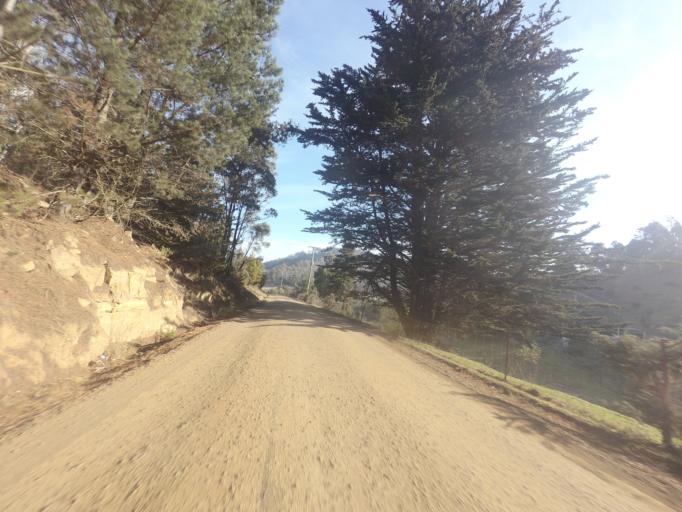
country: AU
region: Tasmania
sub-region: Sorell
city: Sorell
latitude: -42.4881
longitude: 147.4344
